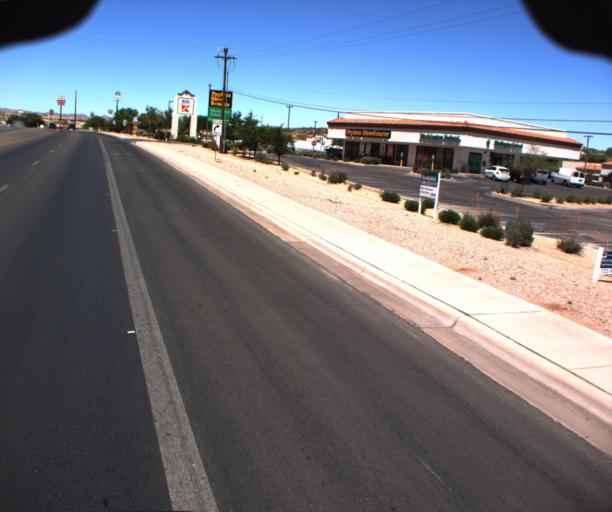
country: US
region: Arizona
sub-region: Santa Cruz County
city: Nogales
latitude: 31.3671
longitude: -110.9343
